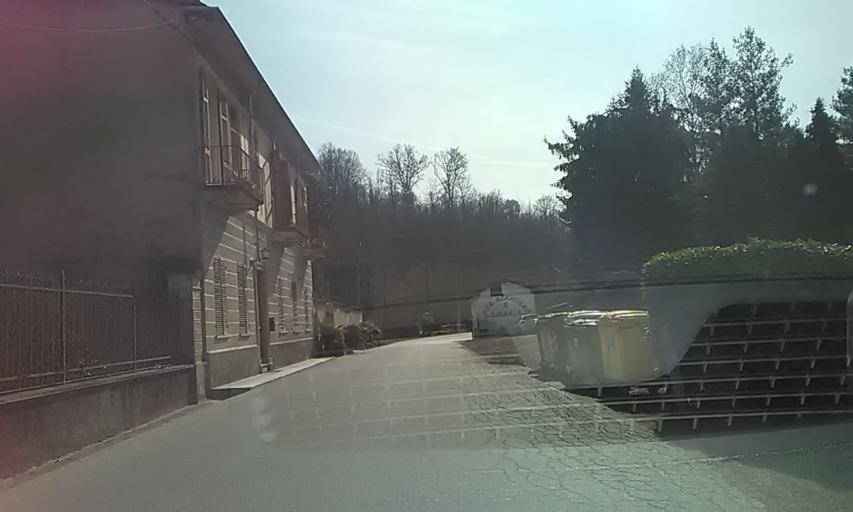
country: IT
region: Piedmont
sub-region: Provincia di Biella
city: Brusnengo
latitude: 45.6045
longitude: 8.2419
